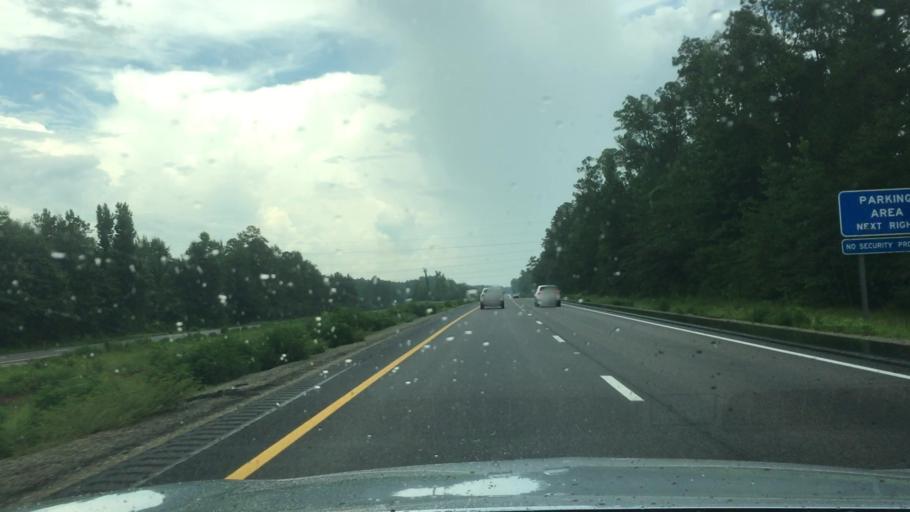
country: US
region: Mississippi
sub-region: Lamar County
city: Purvis
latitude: 31.1914
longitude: -89.3416
